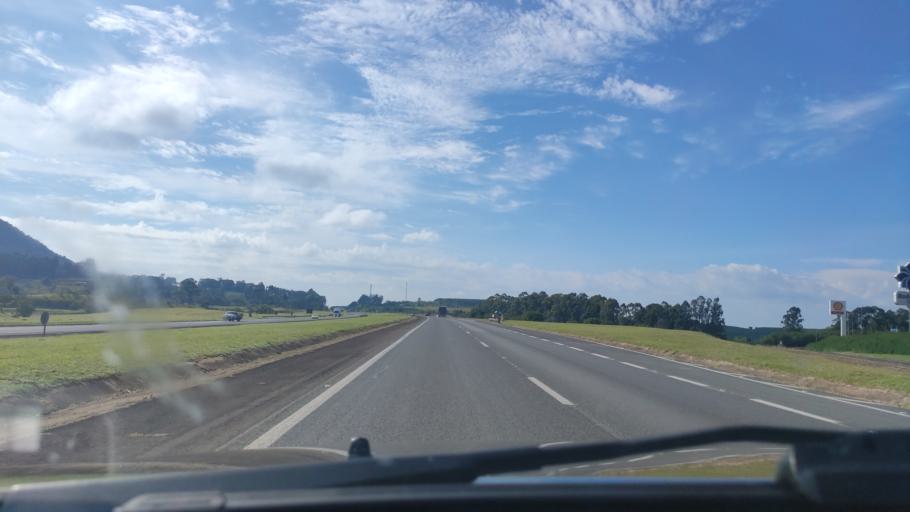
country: BR
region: Sao Paulo
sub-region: Itatinga
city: Itatinga
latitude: -23.1562
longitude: -48.3781
